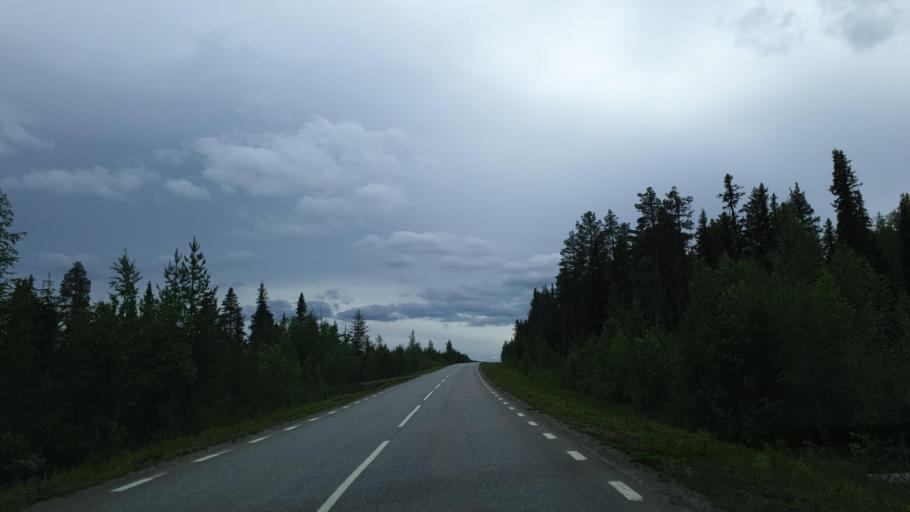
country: SE
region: Vaesterbotten
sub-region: Sorsele Kommun
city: Sorsele
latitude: 65.5374
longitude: 17.3970
